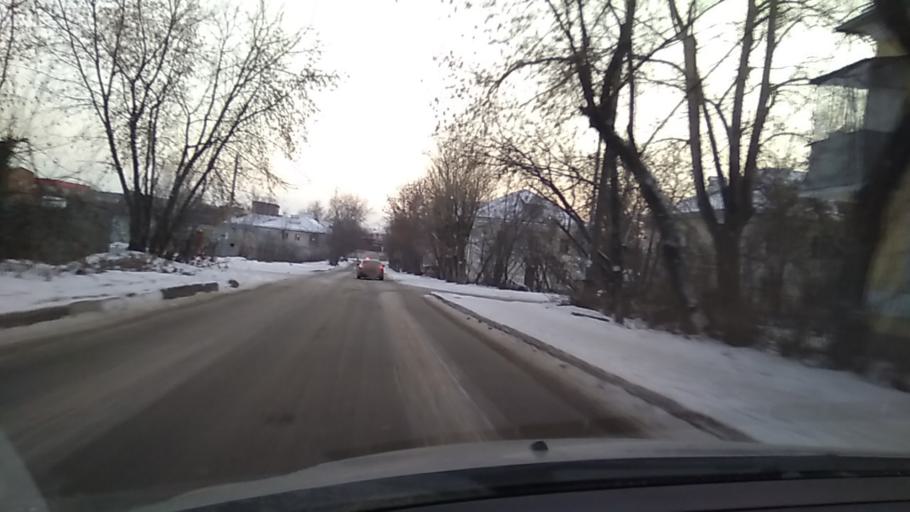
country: RU
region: Sverdlovsk
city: Istok
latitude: 56.7608
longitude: 60.7117
